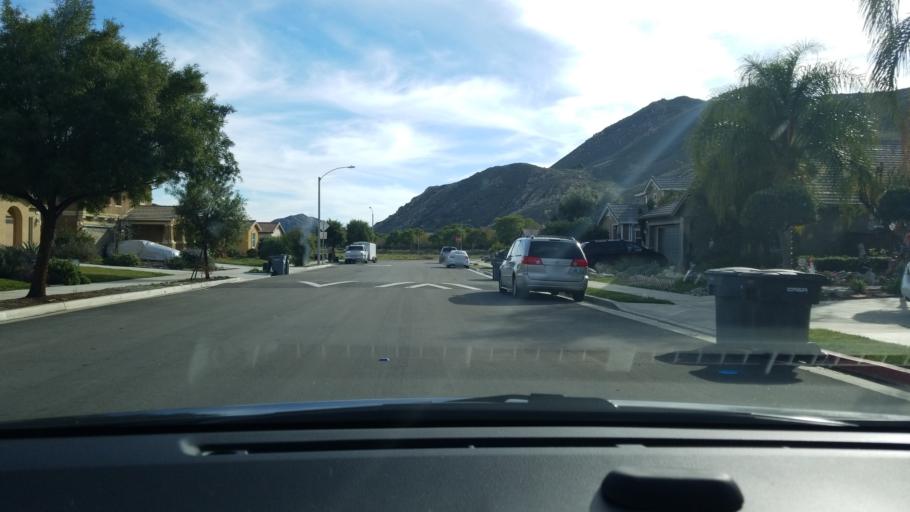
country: US
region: California
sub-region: Riverside County
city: Green Acres
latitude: 33.7939
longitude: -117.0373
